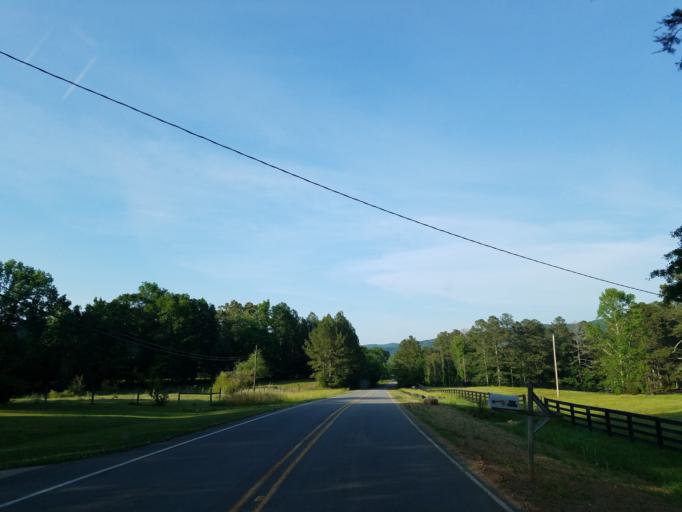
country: US
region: Georgia
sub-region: Floyd County
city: Shannon
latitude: 34.4914
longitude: -85.1275
